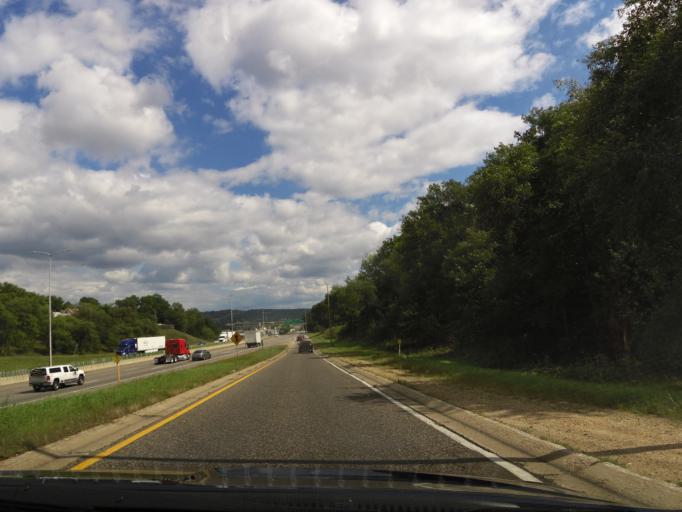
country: US
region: Minnesota
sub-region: Dakota County
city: South Saint Paul
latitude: 44.8740
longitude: -93.0395
